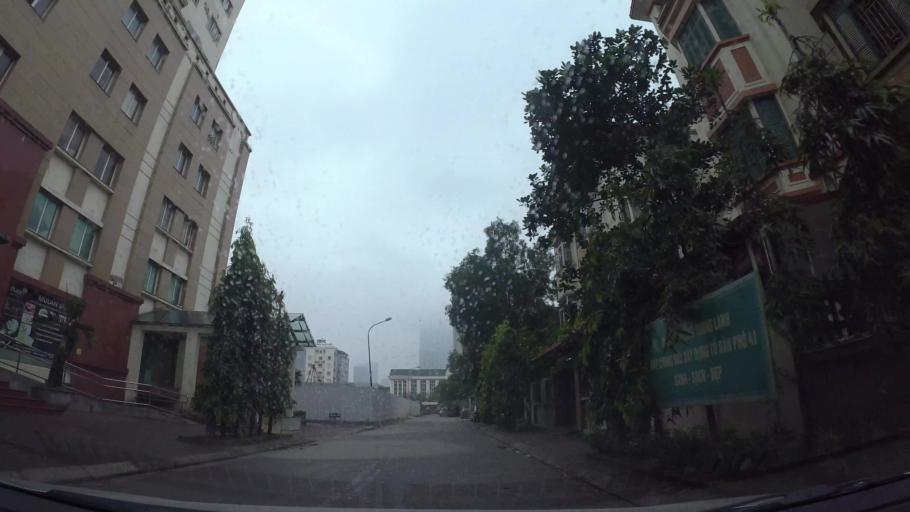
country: VN
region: Ha Noi
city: Thanh Xuan
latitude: 21.0089
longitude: 105.7907
